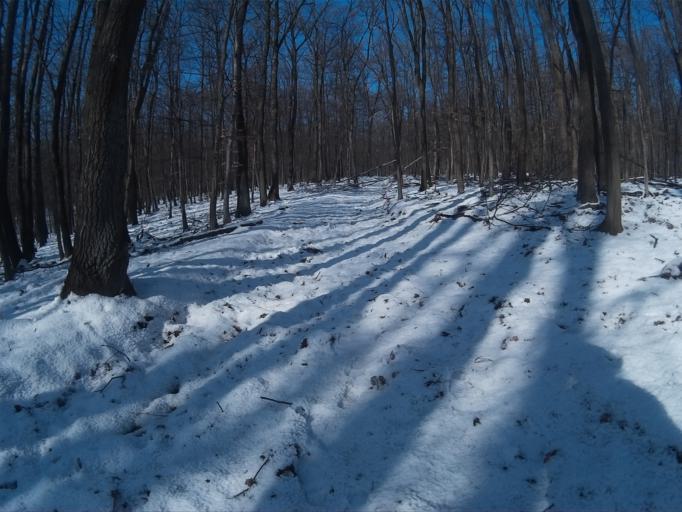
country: HU
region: Komarom-Esztergom
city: Labatlan
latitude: 47.6976
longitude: 18.5167
